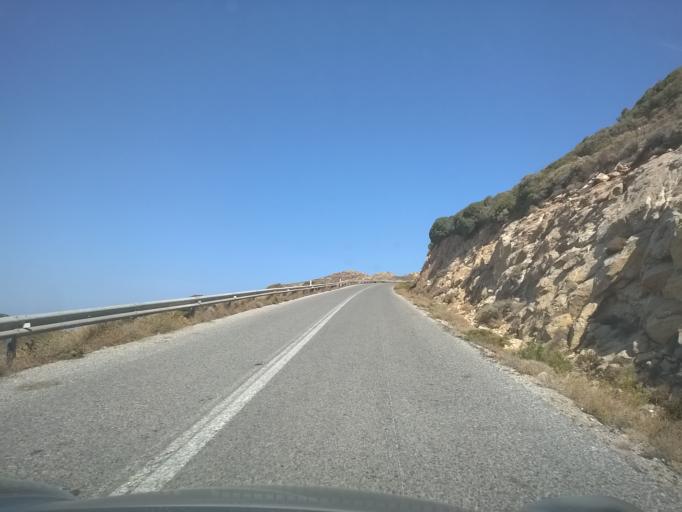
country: GR
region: South Aegean
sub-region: Nomos Kykladon
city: Filotion
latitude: 37.0940
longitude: 25.4662
